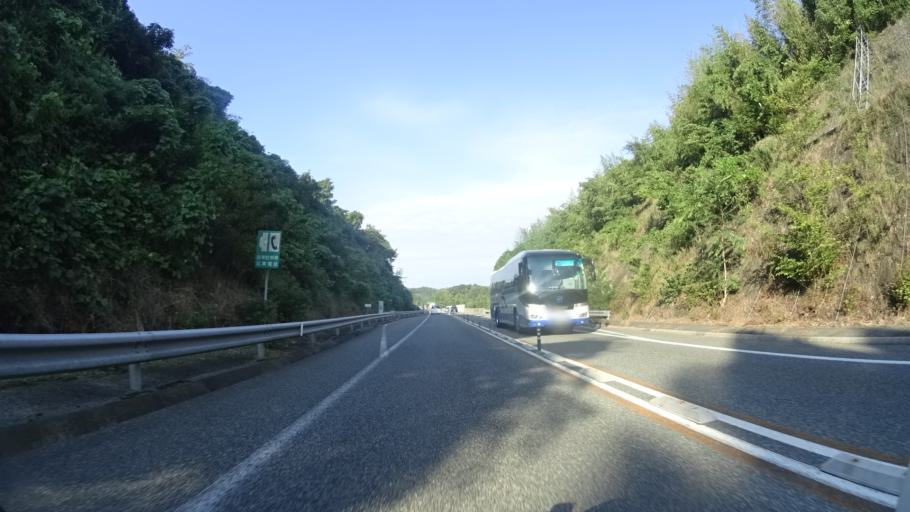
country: JP
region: Shimane
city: Matsue-shi
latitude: 35.4114
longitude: 132.9500
